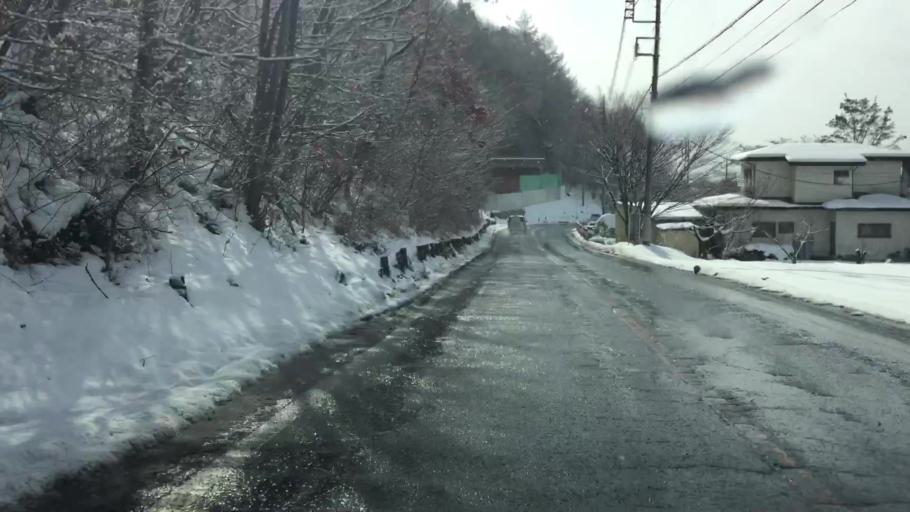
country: JP
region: Gunma
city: Numata
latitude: 36.6780
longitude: 139.0636
